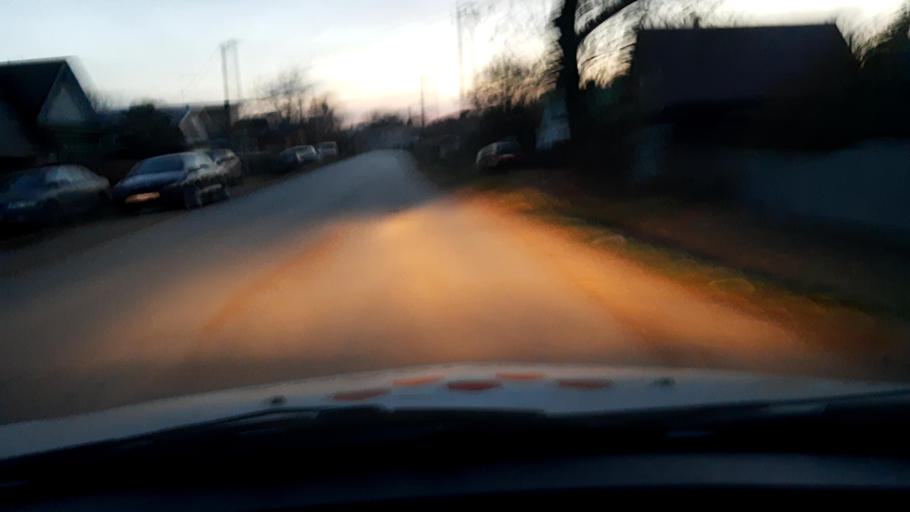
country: RU
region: Bashkortostan
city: Iglino
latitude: 54.7628
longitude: 56.2311
